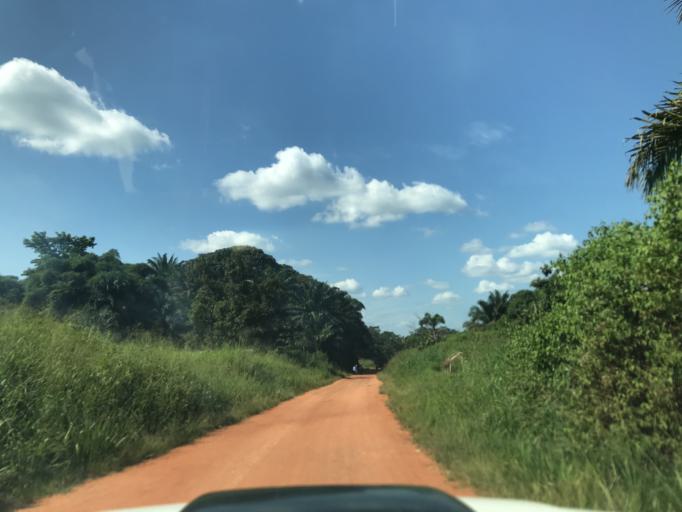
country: CD
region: Eastern Province
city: Kisangani
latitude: 1.2023
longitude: 25.2577
